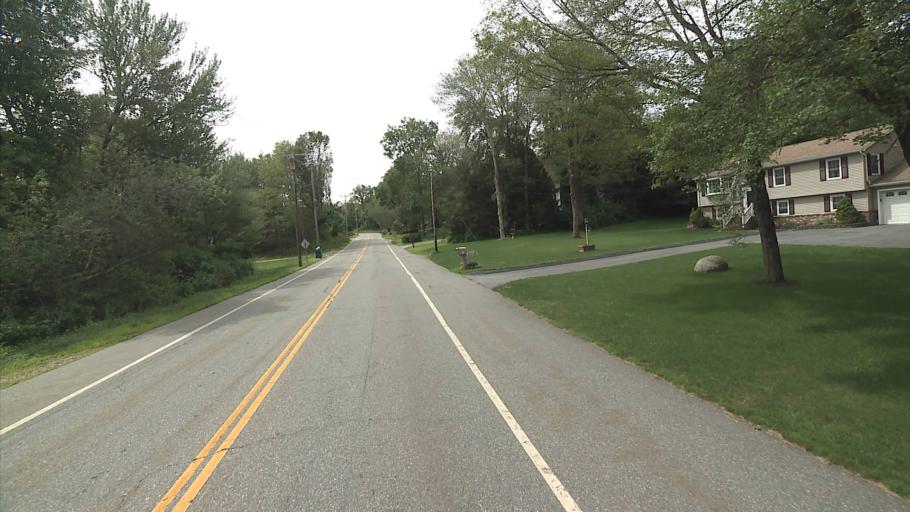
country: US
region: Connecticut
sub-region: Windham County
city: Thompson
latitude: 41.9884
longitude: -71.8434
